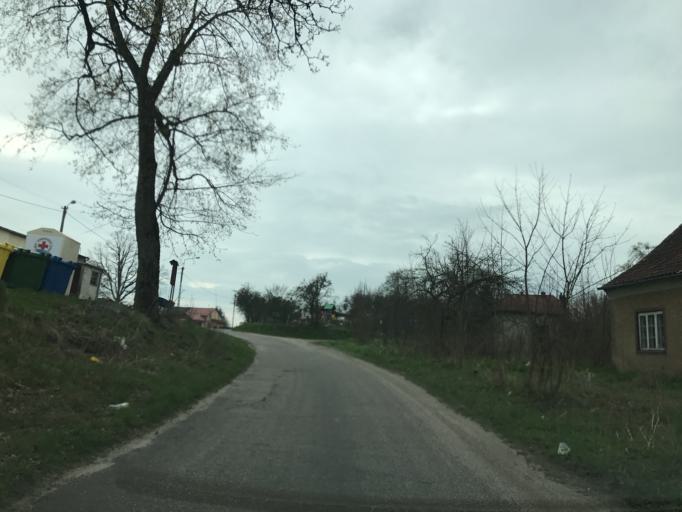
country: PL
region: Warmian-Masurian Voivodeship
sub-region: Powiat olsztynski
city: Olsztynek
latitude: 53.6262
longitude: 20.2199
